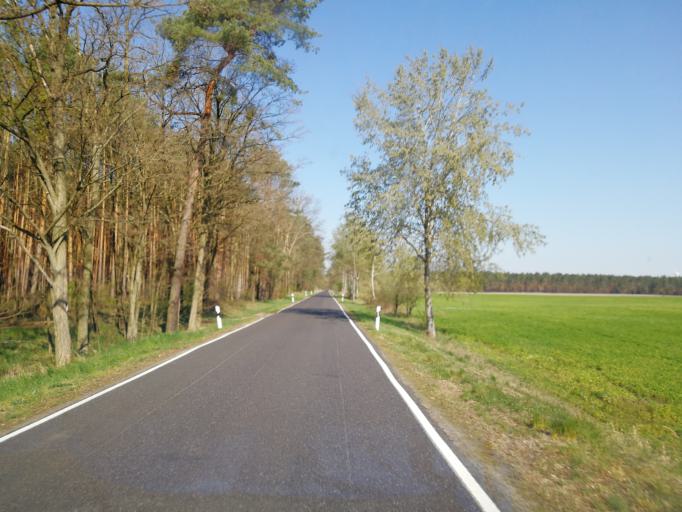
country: DE
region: Brandenburg
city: Bronkow
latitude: 51.7085
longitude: 13.8721
